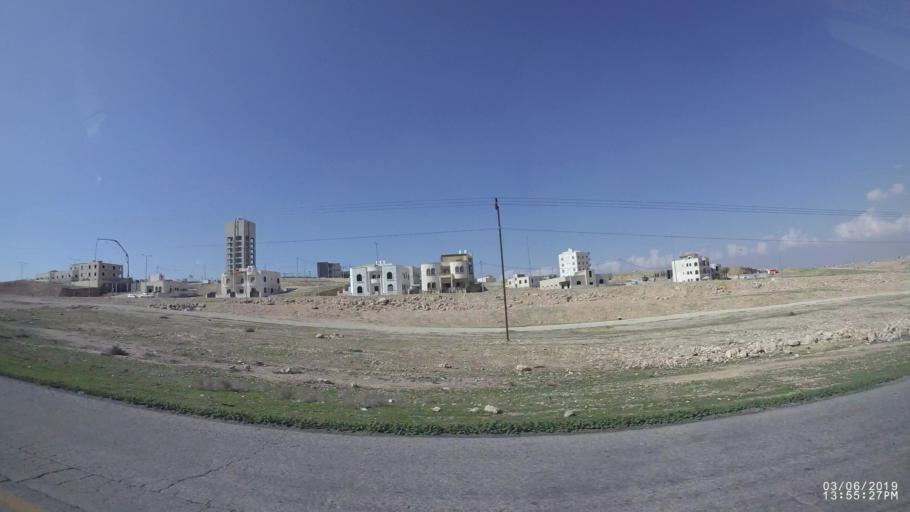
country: JO
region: Zarqa
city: Zarqa
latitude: 32.0473
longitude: 36.1214
